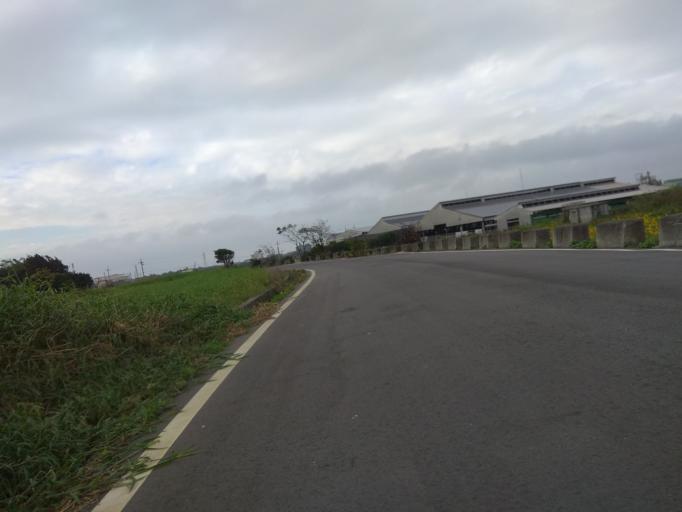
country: TW
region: Taiwan
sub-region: Hsinchu
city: Zhubei
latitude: 24.9777
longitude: 121.0375
